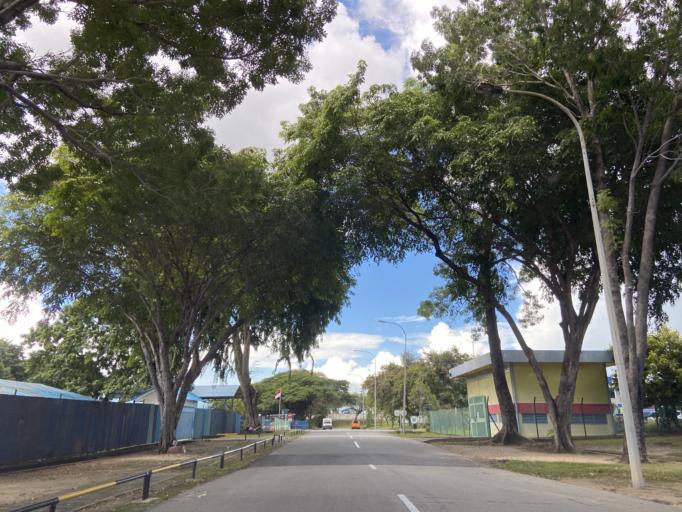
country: SG
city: Singapore
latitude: 1.0635
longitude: 104.0272
